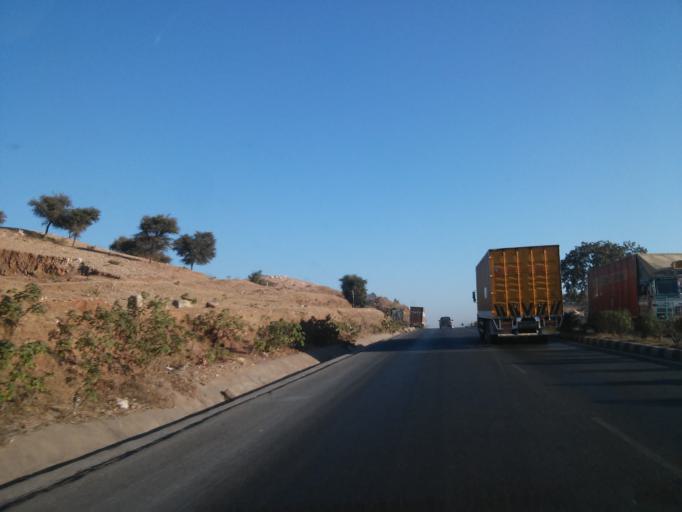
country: IN
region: Rajasthan
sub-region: Dungarpur
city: Dungarpur
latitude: 23.9310
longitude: 73.5689
